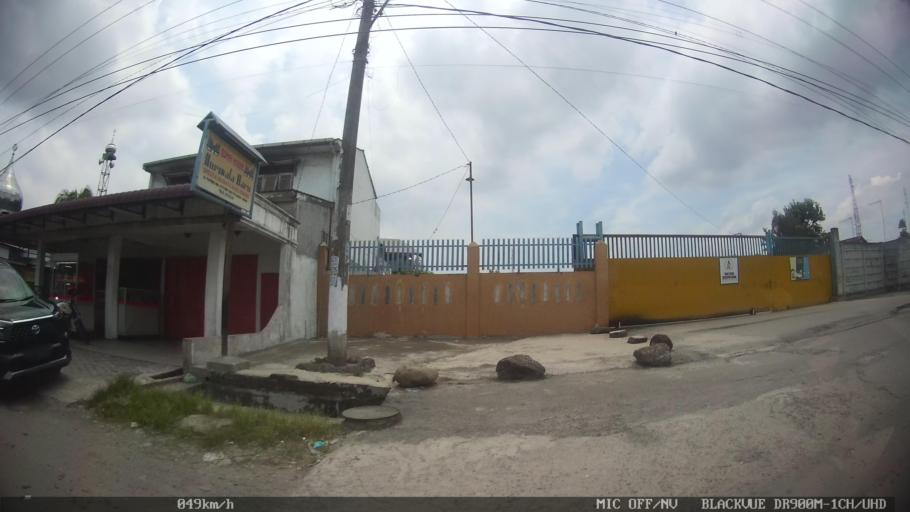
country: ID
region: North Sumatra
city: Labuhan Deli
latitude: 3.6838
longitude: 98.6681
